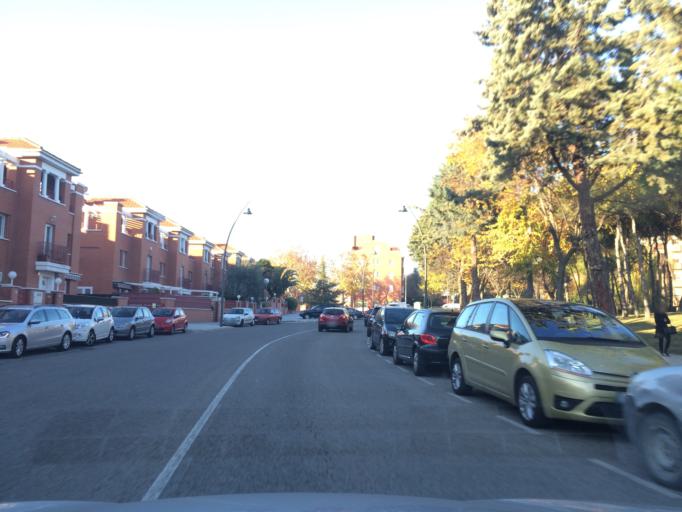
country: ES
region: Madrid
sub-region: Provincia de Madrid
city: Tres Cantos
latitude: 40.5926
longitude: -3.7032
